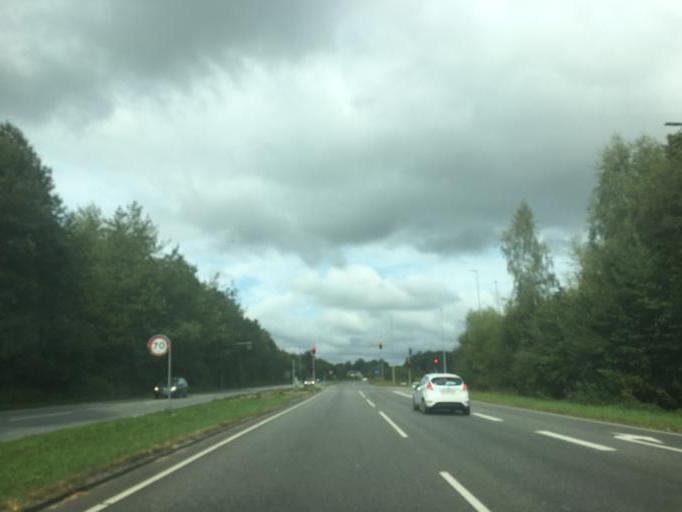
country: DK
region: South Denmark
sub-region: Kolding Kommune
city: Kolding
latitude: 55.5102
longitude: 9.5035
